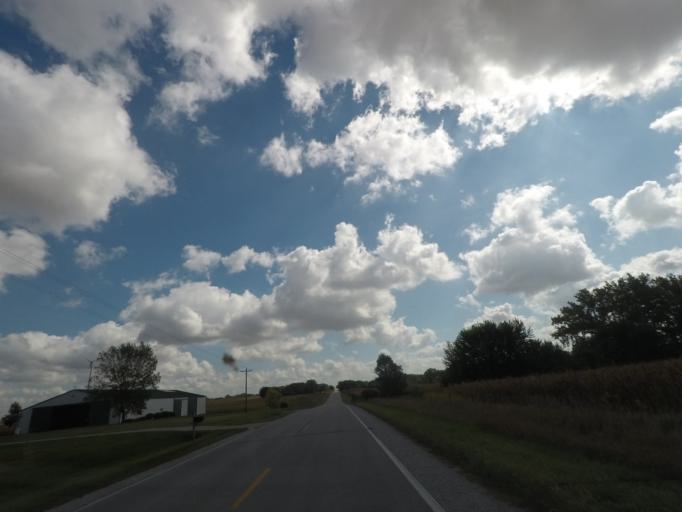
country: US
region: Iowa
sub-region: Story County
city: Nevada
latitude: 42.0227
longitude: -93.3450
